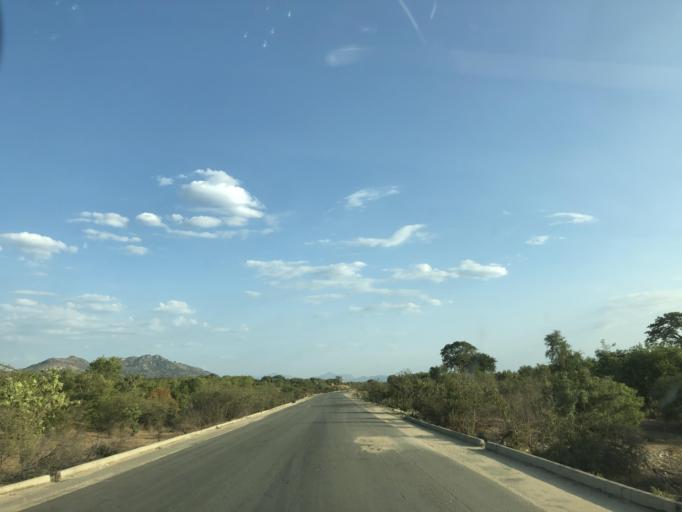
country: AO
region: Huila
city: Caluquembe
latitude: -13.5005
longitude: 13.9151
